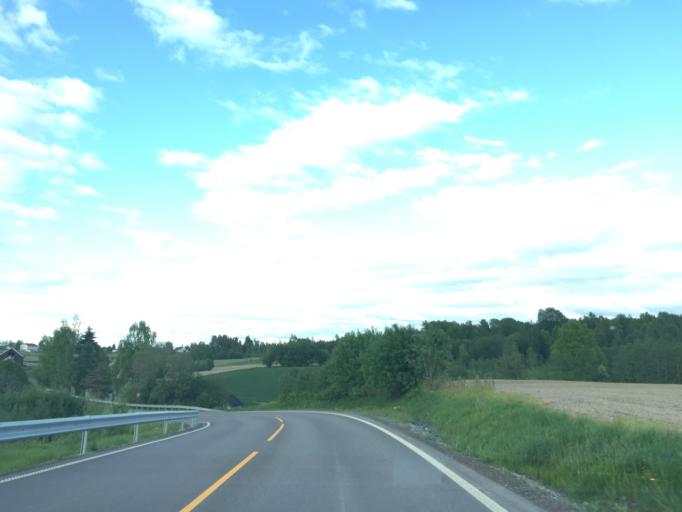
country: NO
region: Akershus
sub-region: Sorum
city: Sorumsand
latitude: 59.9714
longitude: 11.2228
